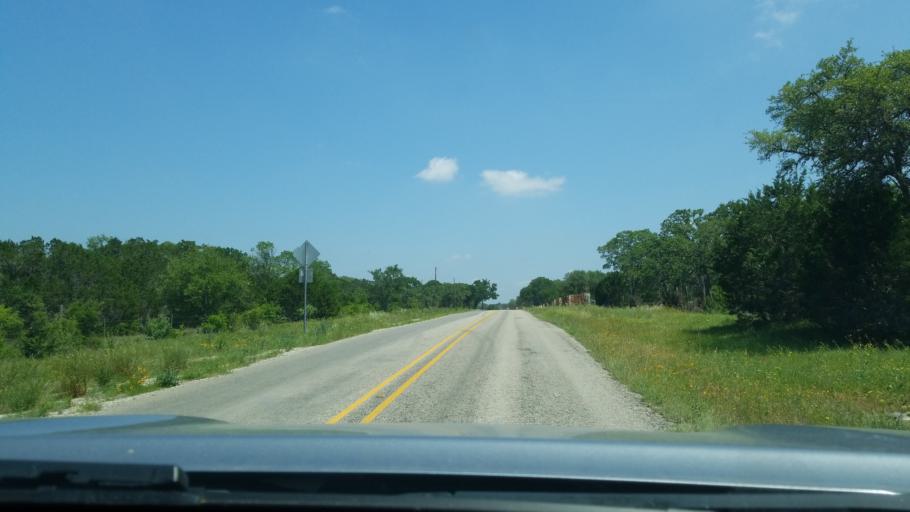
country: US
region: Texas
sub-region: Blanco County
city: Blanco
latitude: 29.9773
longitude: -98.5441
